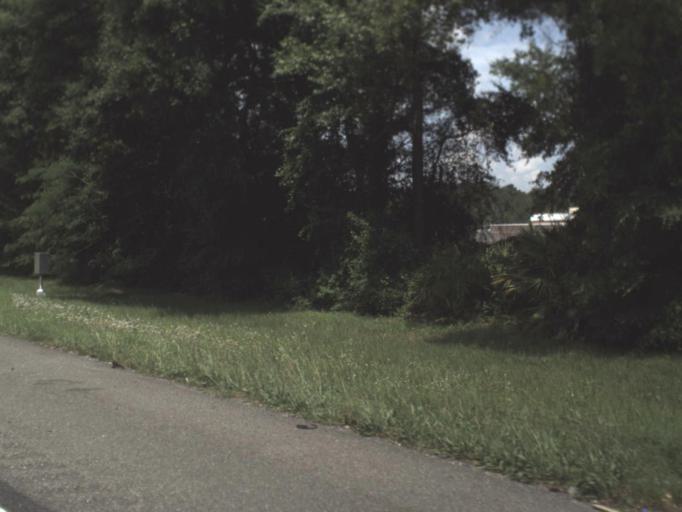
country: US
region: Florida
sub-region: Clay County
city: Bellair-Meadowbrook Terrace
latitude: 30.2880
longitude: -81.7713
